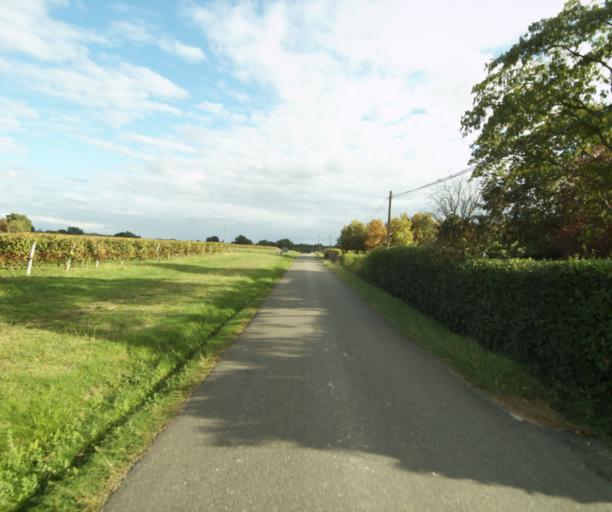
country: FR
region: Midi-Pyrenees
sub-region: Departement du Gers
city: Eauze
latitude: 43.8822
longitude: 0.0772
